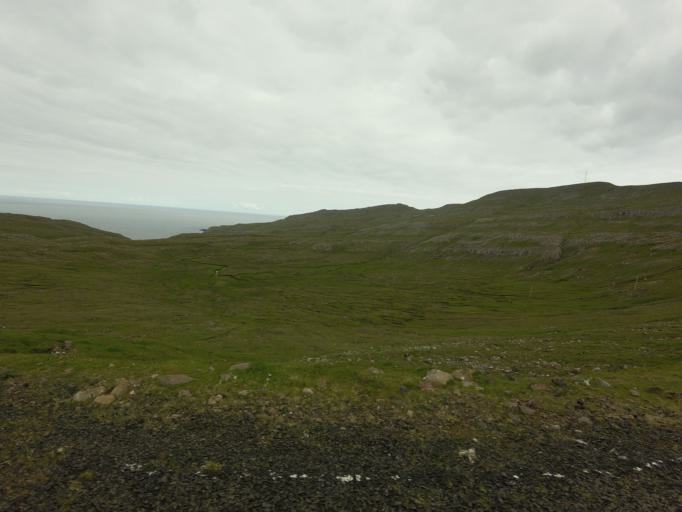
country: FO
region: Suduroy
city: Vagur
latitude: 61.4346
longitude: -6.7561
